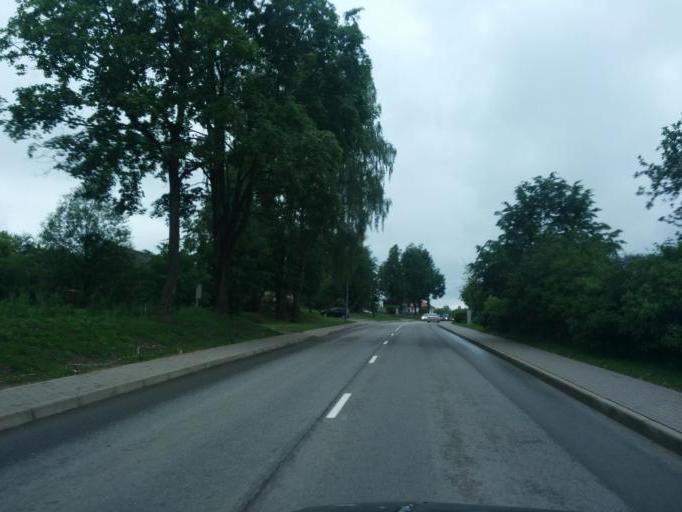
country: LV
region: Smiltene
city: Smiltene
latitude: 57.4276
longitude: 25.8947
